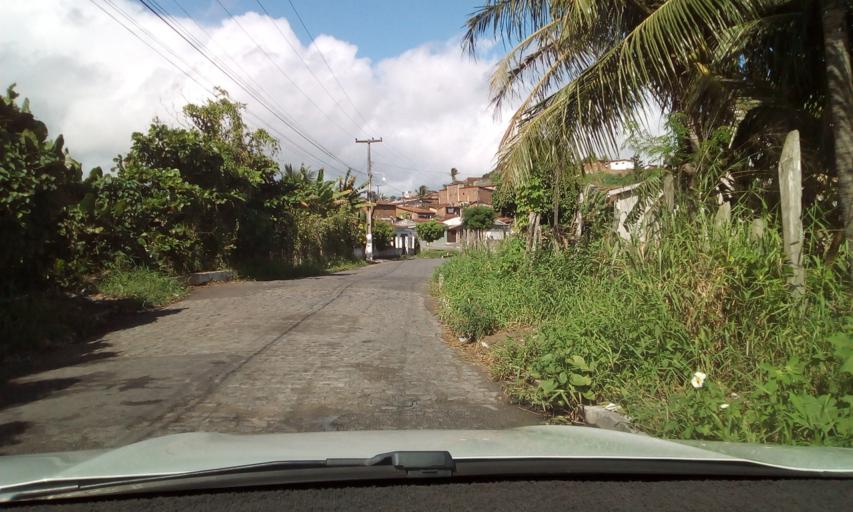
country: BR
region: Paraiba
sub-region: Santa Rita
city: Santa Rita
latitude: -7.1258
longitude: -34.9751
